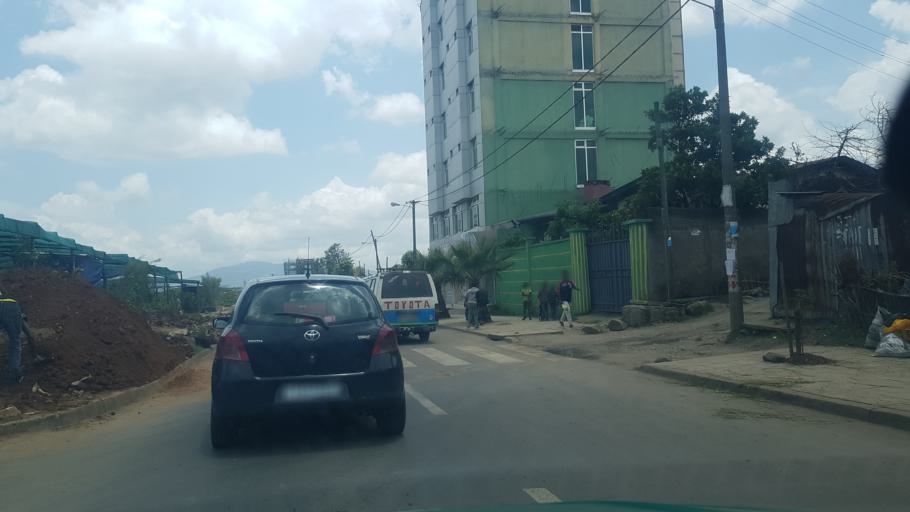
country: ET
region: Adis Abeba
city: Addis Ababa
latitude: 8.9979
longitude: 38.7549
